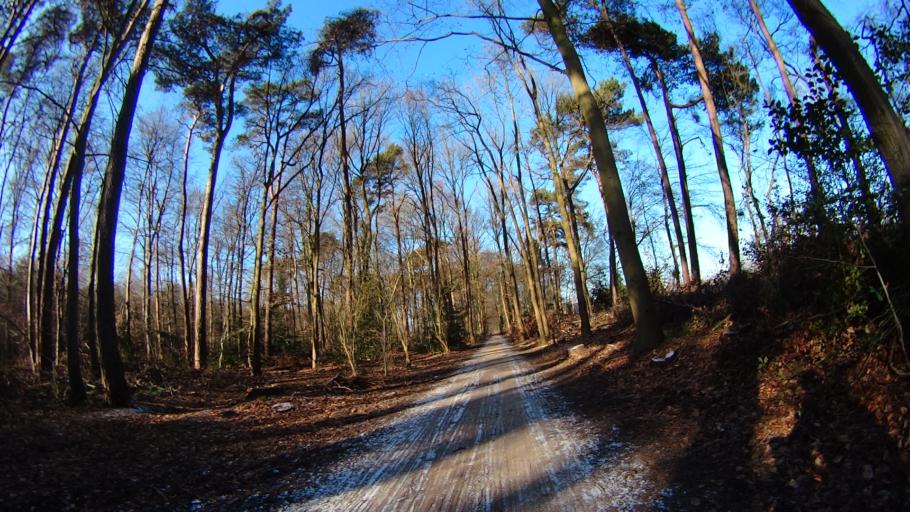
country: NL
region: Utrecht
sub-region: Gemeente Soest
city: Soest
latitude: 52.1671
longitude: 5.2638
